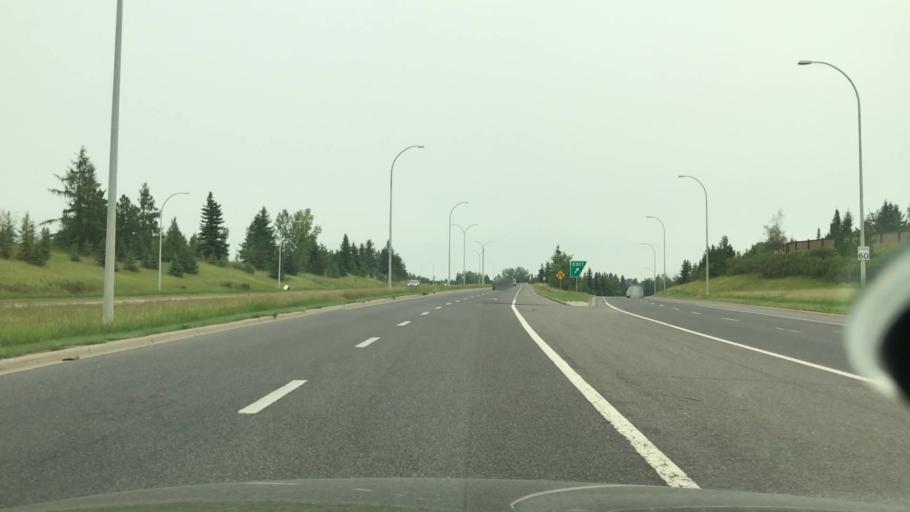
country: CA
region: Alberta
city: Edmonton
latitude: 53.4795
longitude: -113.5723
